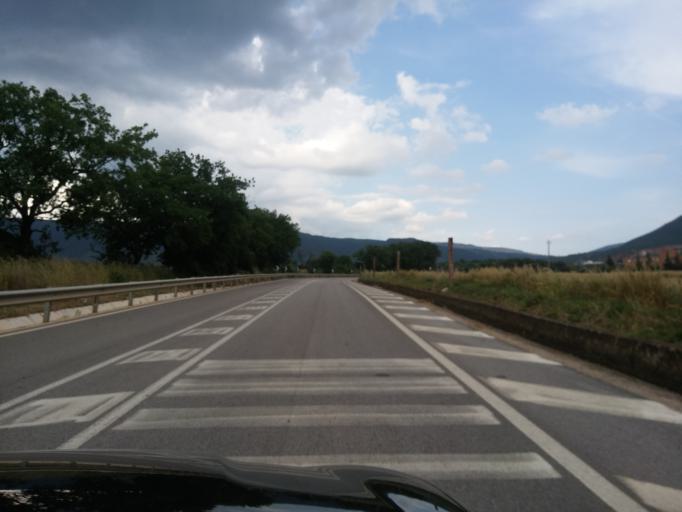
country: IT
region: Apulia
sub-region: Provincia di Foggia
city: Rignano Garganico
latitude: 41.7150
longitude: 15.5363
